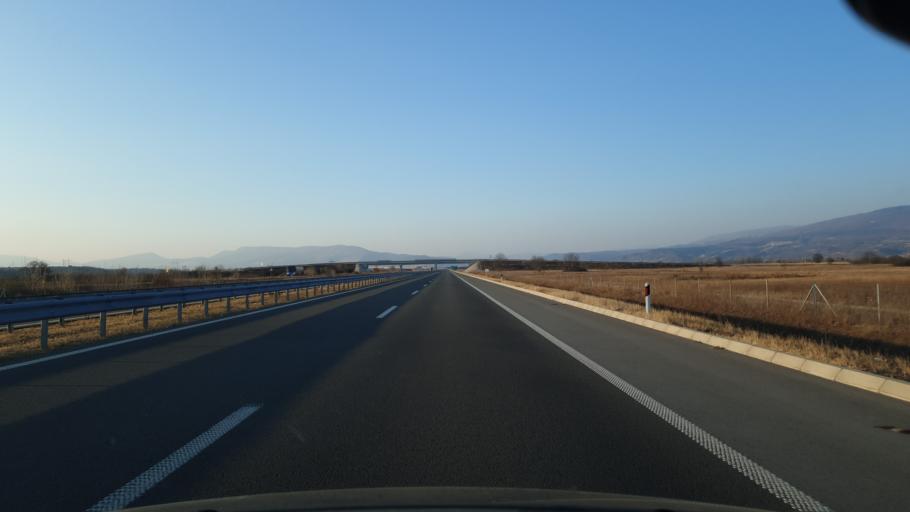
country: RS
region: Central Serbia
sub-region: Pirotski Okrug
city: Pirot
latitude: 43.1035
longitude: 22.6399
